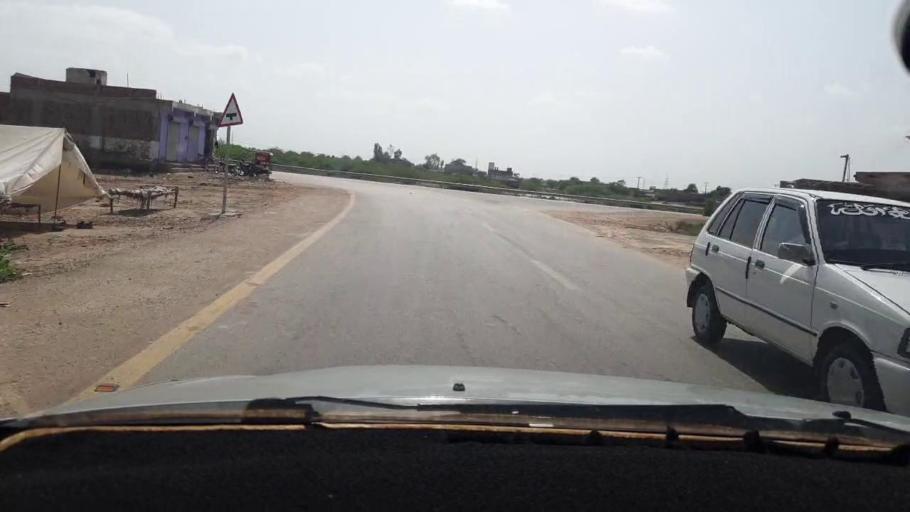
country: PK
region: Sindh
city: Digri
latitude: 25.1454
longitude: 69.1242
